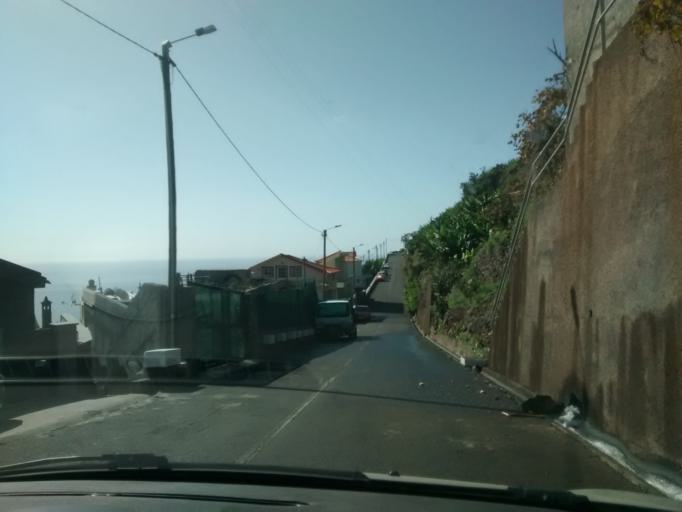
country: PT
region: Madeira
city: Calheta
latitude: 32.7212
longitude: -17.1674
